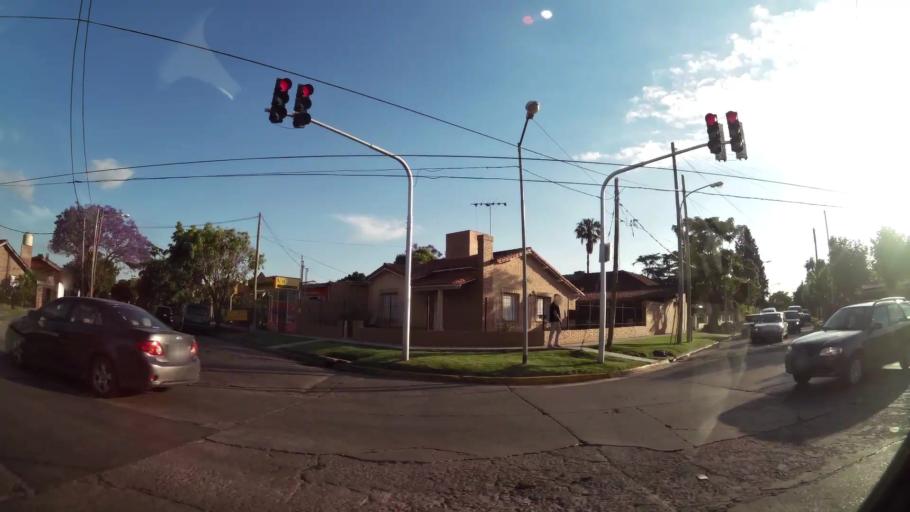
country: AR
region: Buenos Aires
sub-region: Partido de Tigre
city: Tigre
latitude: -34.4554
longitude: -58.6310
